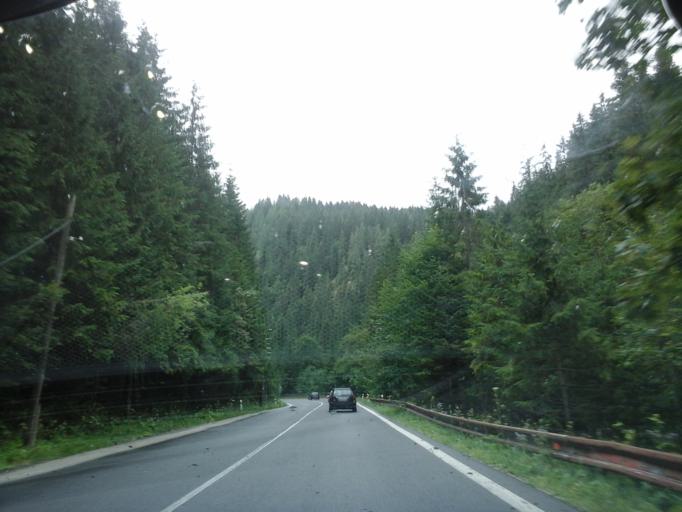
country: SK
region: Kosicky
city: Dobsina
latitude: 48.8846
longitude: 20.3121
